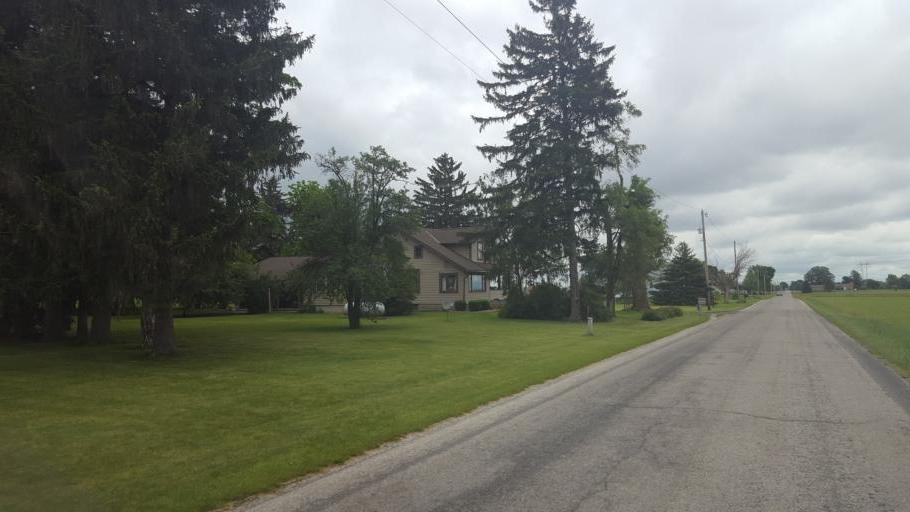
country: US
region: Ohio
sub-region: Crawford County
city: Bucyrus
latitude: 40.7757
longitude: -83.0132
